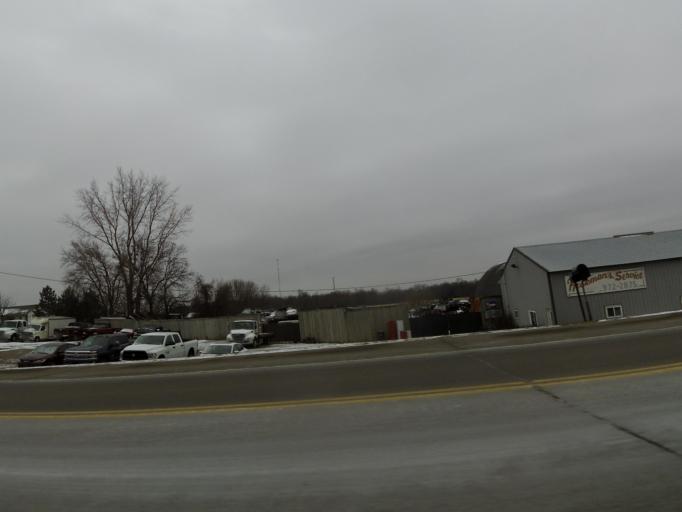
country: US
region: Minnesota
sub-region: Wright County
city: Delano
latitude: 45.0648
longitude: -93.8342
